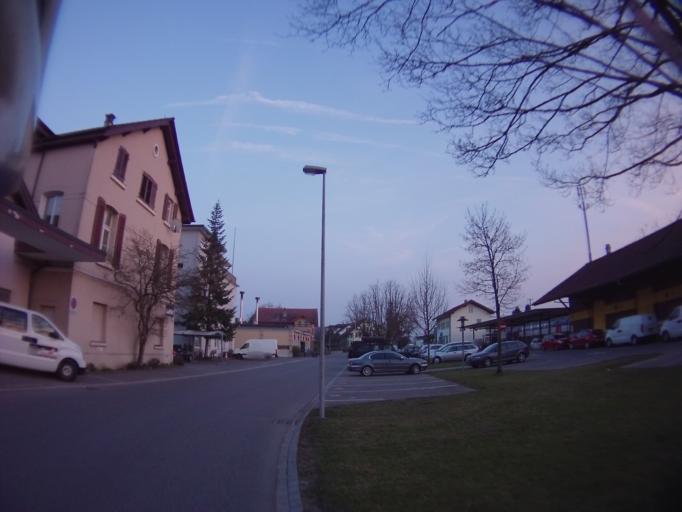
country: CH
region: Zurich
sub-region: Bezirk Affoltern
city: Mettmenstetten
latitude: 47.2451
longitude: 8.4574
